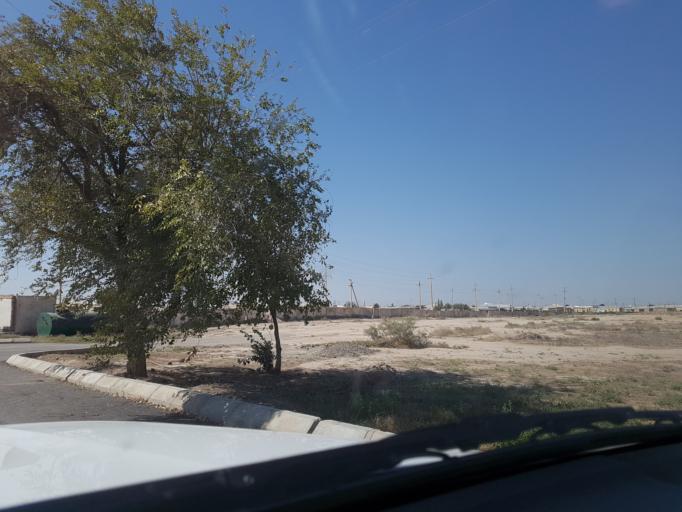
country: IR
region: Razavi Khorasan
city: Sarakhs
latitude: 36.5136
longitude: 61.2263
